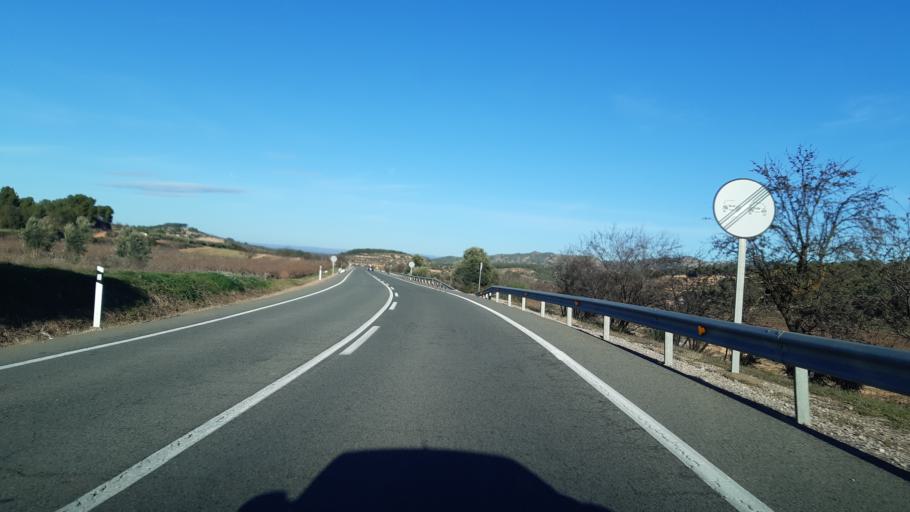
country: ES
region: Catalonia
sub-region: Provincia de Tarragona
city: Gandesa
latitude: 41.0870
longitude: 0.5108
